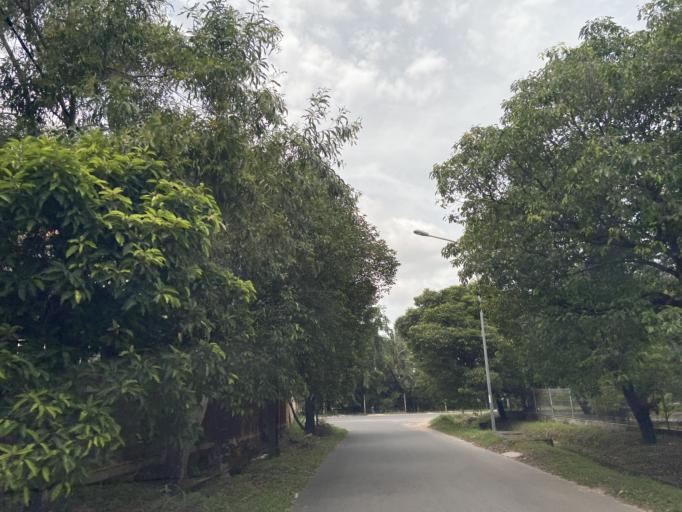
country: SG
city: Singapore
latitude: 1.1608
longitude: 104.0114
